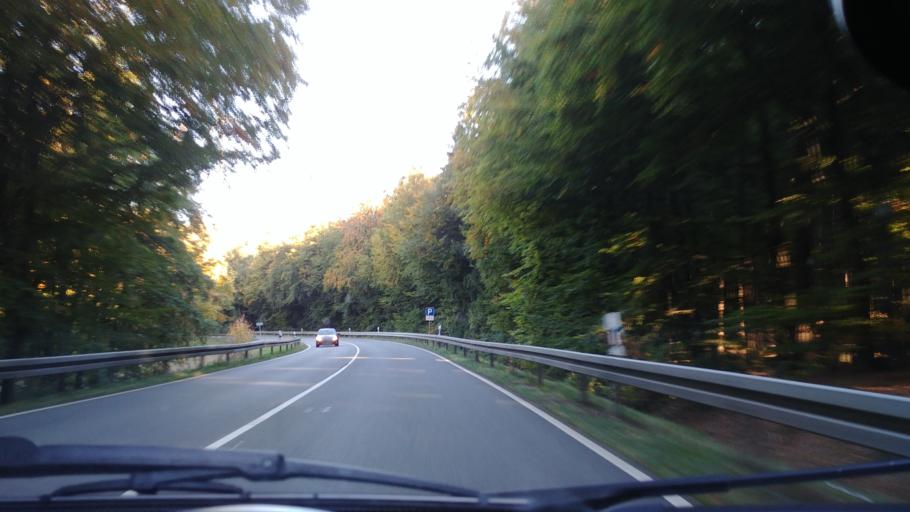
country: DE
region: Rheinland-Pfalz
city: Rettert
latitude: 50.2041
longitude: 7.9525
